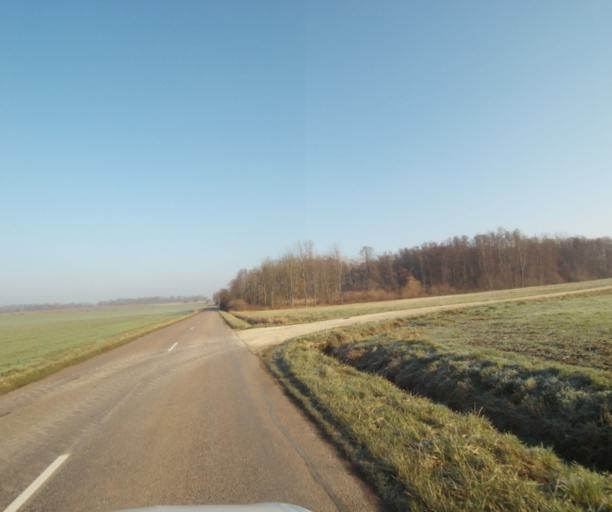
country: FR
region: Champagne-Ardenne
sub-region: Departement de la Haute-Marne
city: Montier-en-Der
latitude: 48.4192
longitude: 4.7443
